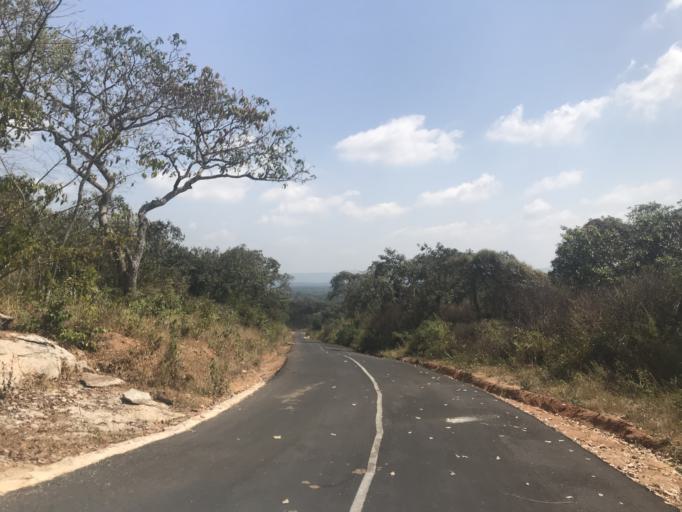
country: NG
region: Osun
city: Otan Ayegbaju
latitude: 7.8947
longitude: 4.8436
